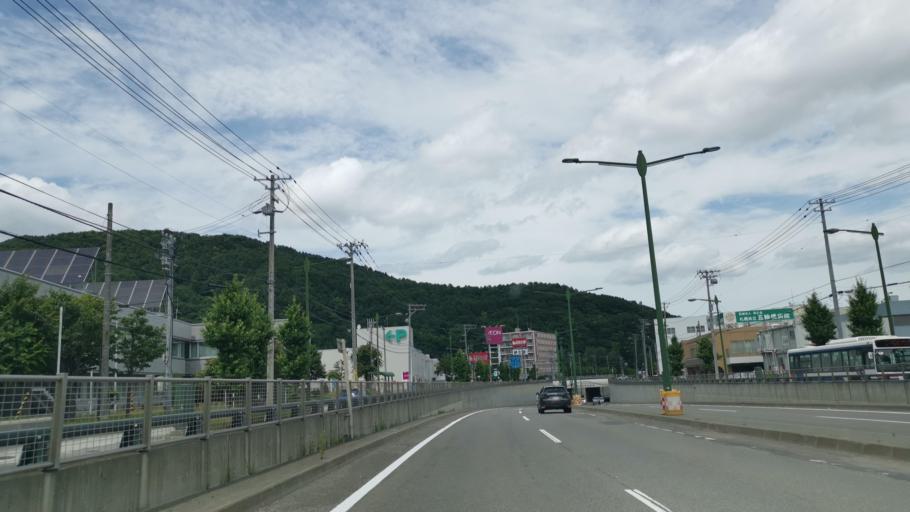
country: JP
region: Hokkaido
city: Sapporo
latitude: 42.9976
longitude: 141.3366
